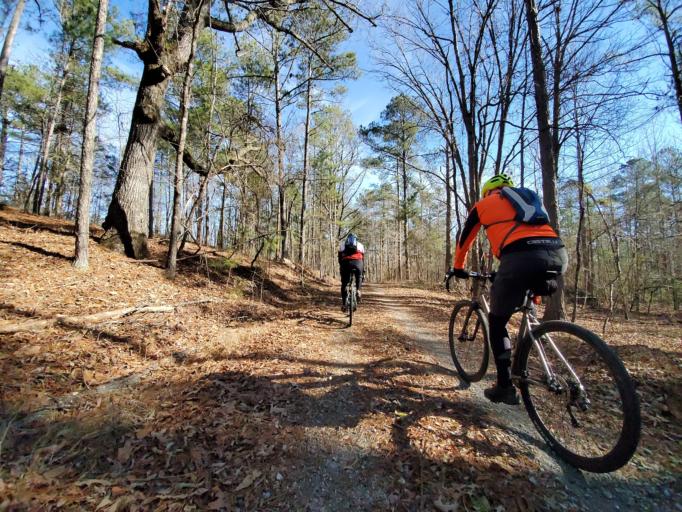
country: US
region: Georgia
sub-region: Fulton County
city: Chattahoochee Hills
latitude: 33.5674
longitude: -84.7409
